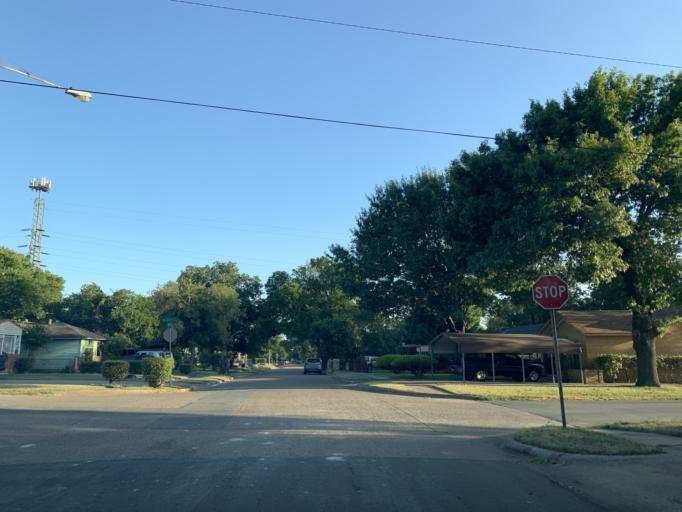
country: US
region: Texas
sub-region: Dallas County
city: Dallas
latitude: 32.7032
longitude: -96.8095
